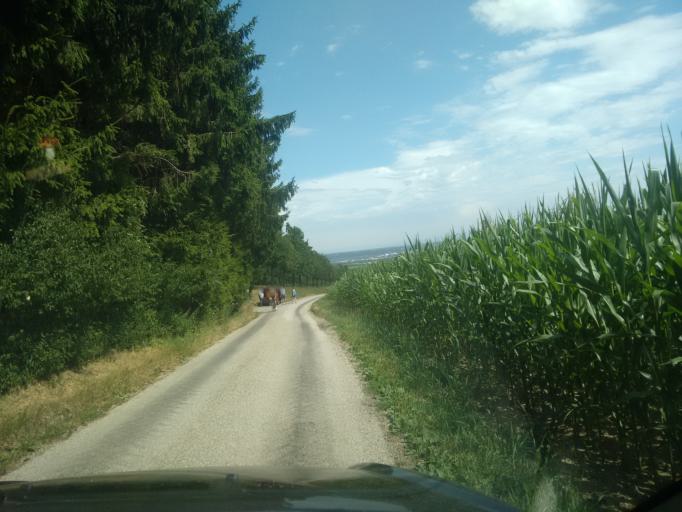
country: AT
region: Upper Austria
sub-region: Wels-Land
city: Gunskirchen
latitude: 48.1727
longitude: 13.9308
